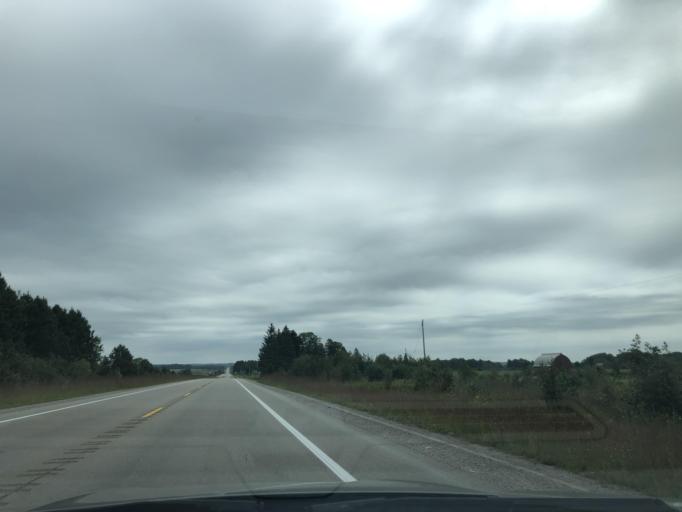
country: US
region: Michigan
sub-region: Clare County
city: Harrison
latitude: 44.0311
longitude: -84.9560
